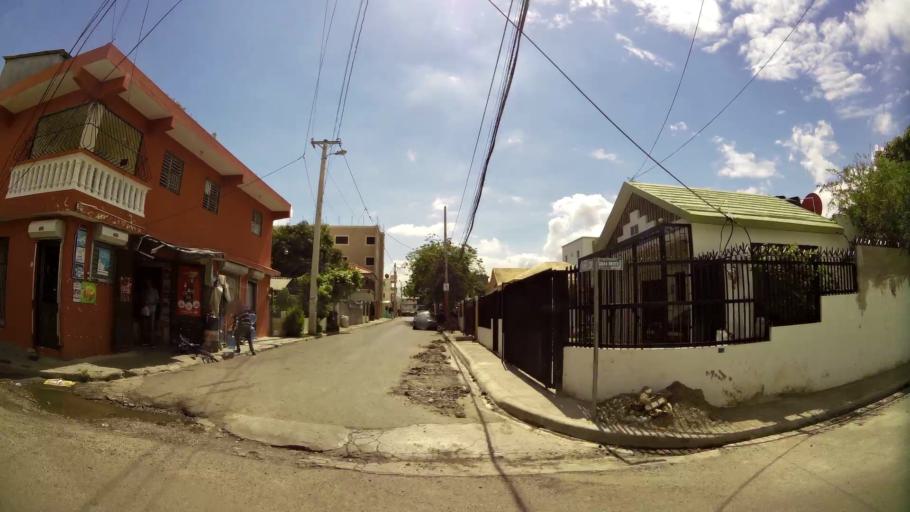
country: DO
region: Santiago
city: Santiago de los Caballeros
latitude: 19.4719
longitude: -70.6990
